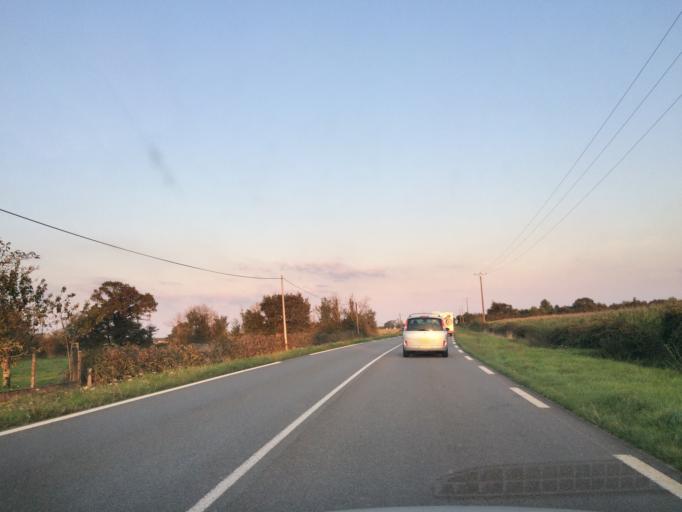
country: FR
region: Pays de la Loire
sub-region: Departement de la Loire-Atlantique
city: Port-Saint-Pere
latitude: 47.1340
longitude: -1.7795
